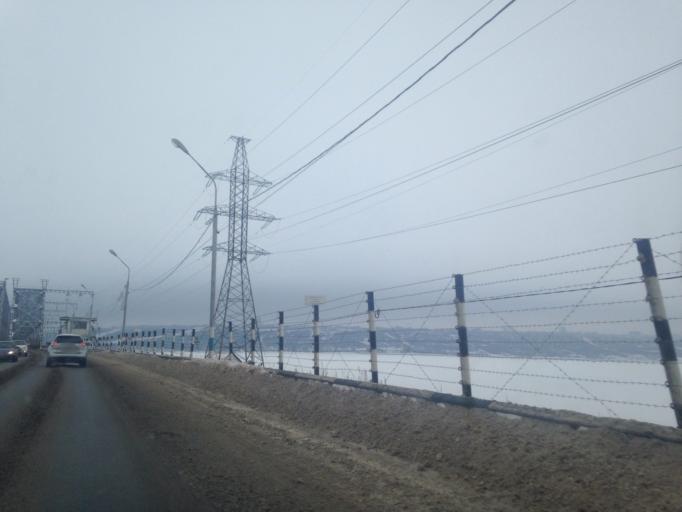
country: RU
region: Ulyanovsk
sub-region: Ulyanovskiy Rayon
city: Ulyanovsk
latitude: 54.3197
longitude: 48.4597
